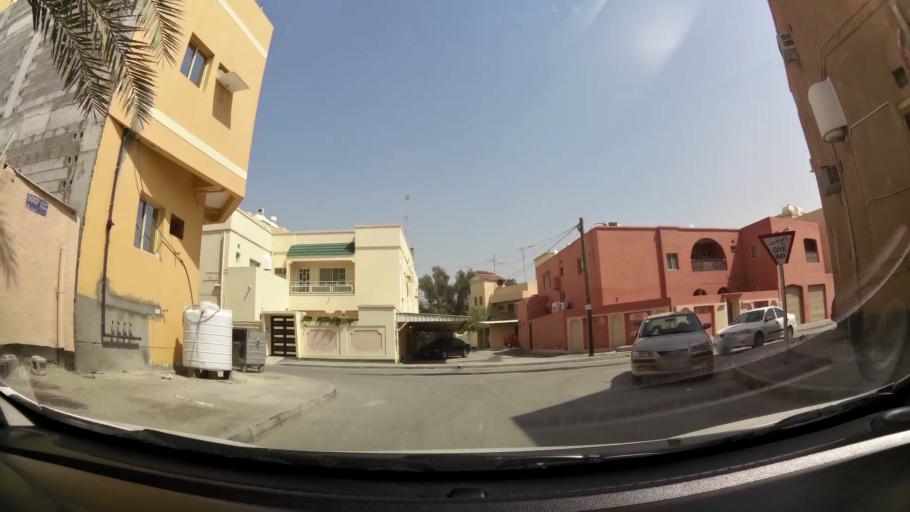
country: BH
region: Manama
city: Jidd Hafs
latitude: 26.2161
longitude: 50.4517
